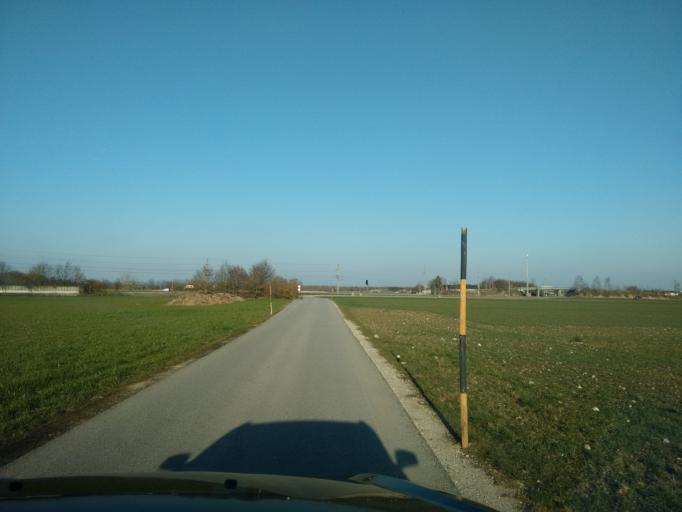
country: AT
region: Upper Austria
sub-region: Wels-Land
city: Marchtrenk
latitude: 48.2065
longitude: 14.1356
